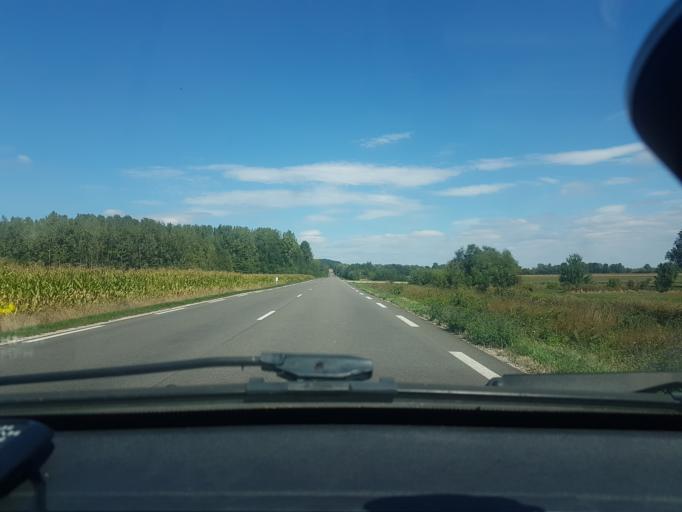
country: FR
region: Franche-Comte
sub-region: Departement de la Haute-Saone
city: Gray-la-Ville
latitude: 47.4341
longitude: 5.5400
